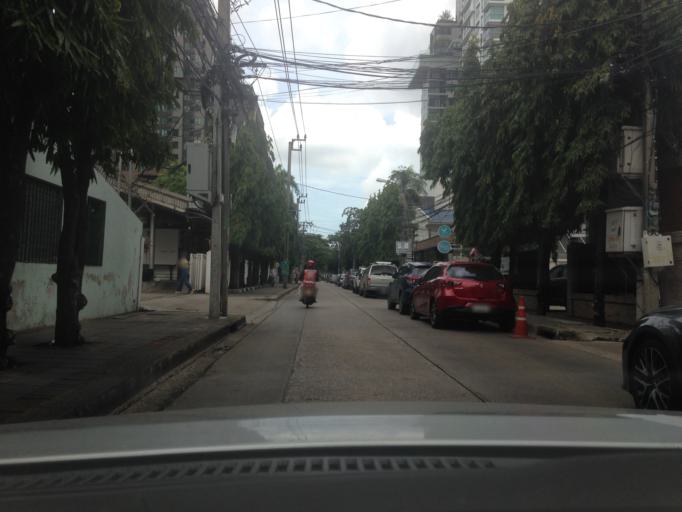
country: TH
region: Bangkok
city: Phaya Thai
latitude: 13.7796
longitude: 100.5434
